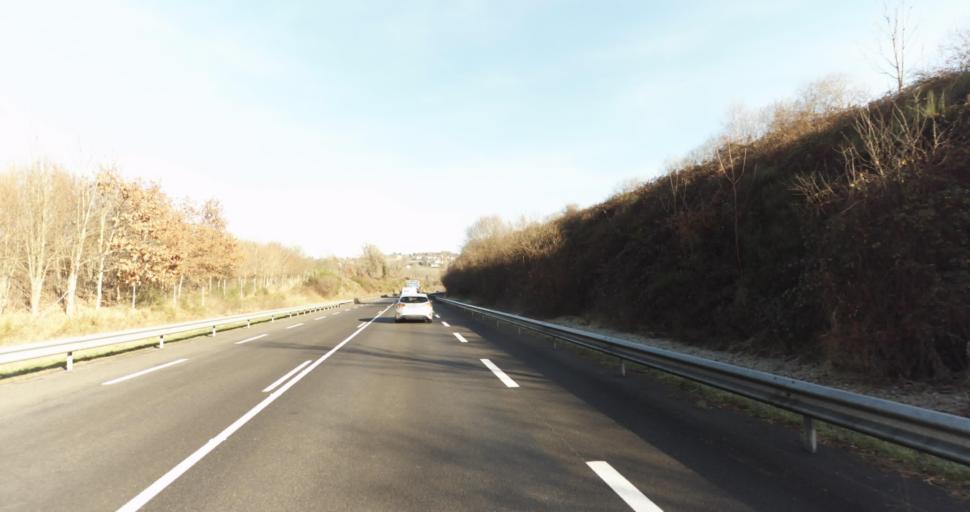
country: FR
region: Limousin
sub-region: Departement de la Haute-Vienne
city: Aixe-sur-Vienne
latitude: 45.8237
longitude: 1.1305
